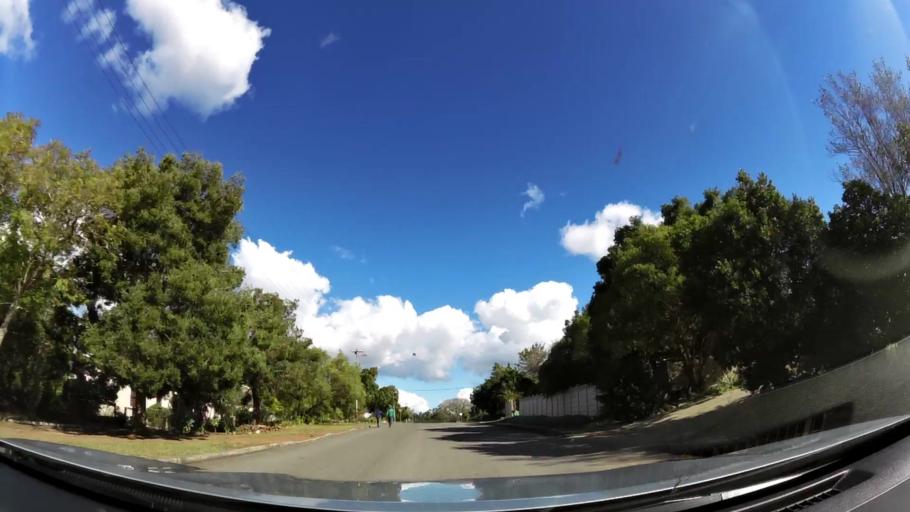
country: ZA
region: Western Cape
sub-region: Overberg District Municipality
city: Swellendam
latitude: -34.0236
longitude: 20.4335
